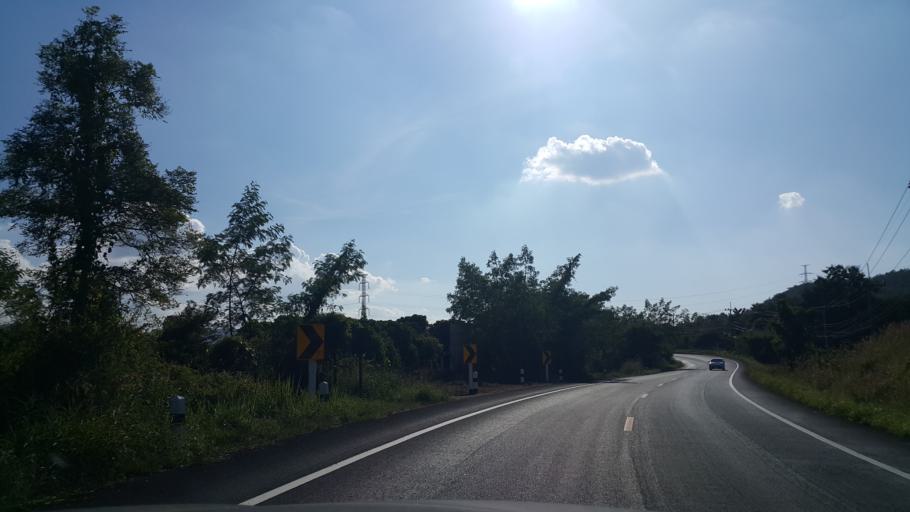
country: TH
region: Lamphun
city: Mae Tha
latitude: 18.4765
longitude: 99.1703
